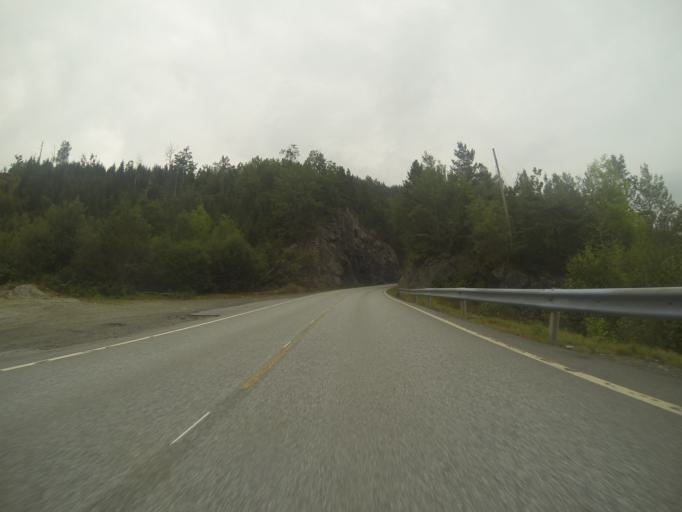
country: NO
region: Rogaland
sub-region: Suldal
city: Sand
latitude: 59.5099
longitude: 6.2138
